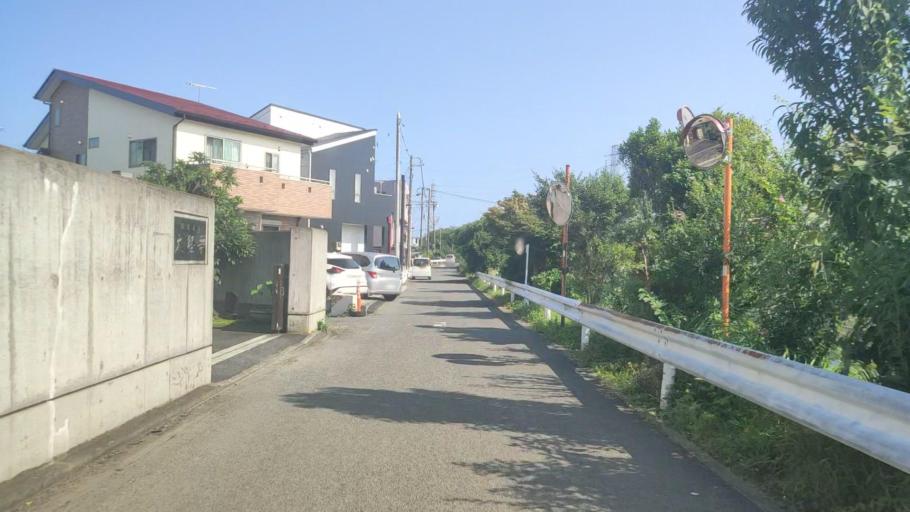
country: JP
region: Kanagawa
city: Hiratsuka
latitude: 35.3519
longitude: 139.3237
